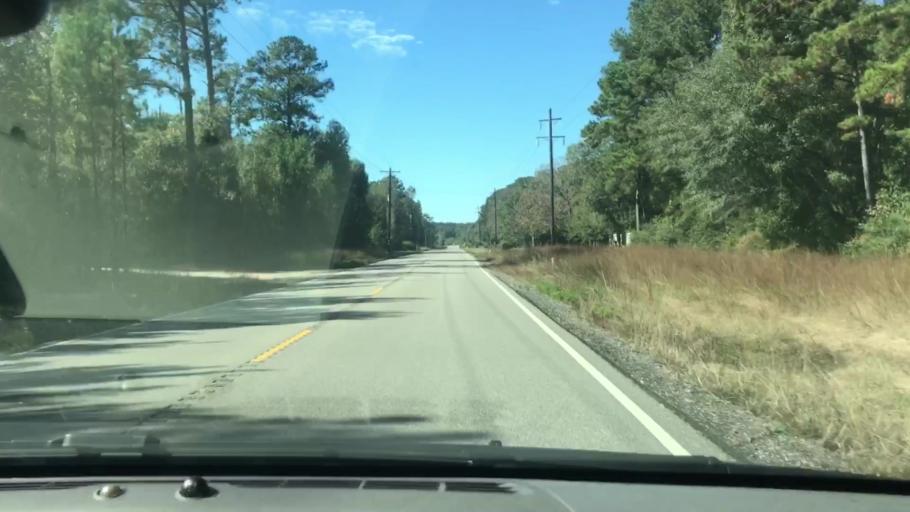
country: US
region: Louisiana
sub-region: Saint Tammany Parish
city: Abita Springs
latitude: 30.5346
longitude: -89.8915
